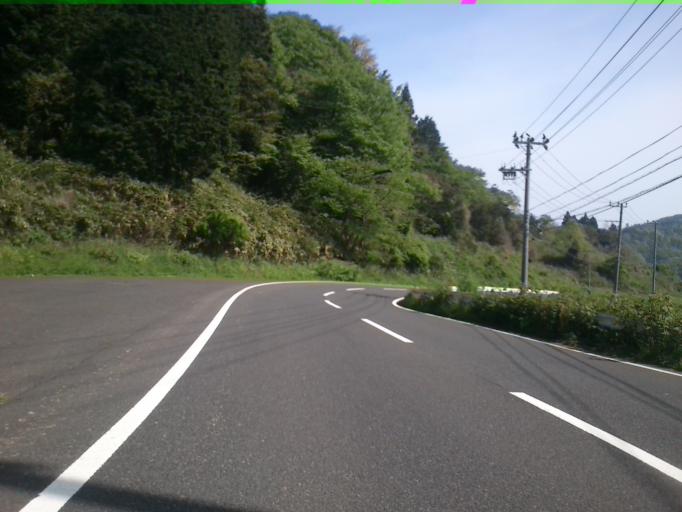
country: JP
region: Kyoto
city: Miyazu
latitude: 35.6806
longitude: 135.2505
